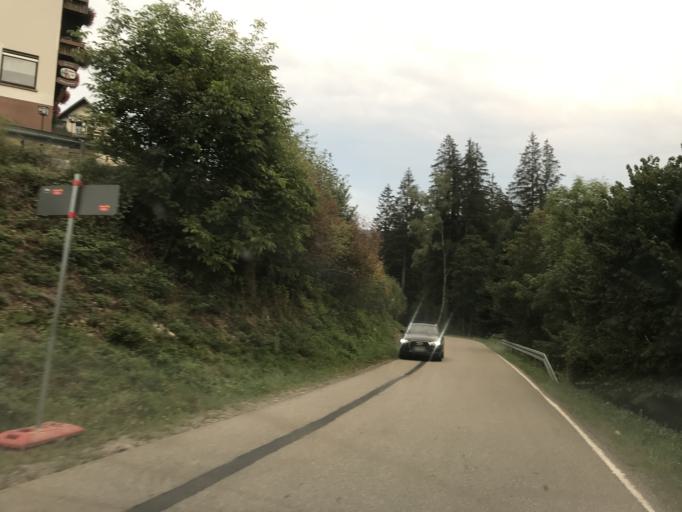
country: DE
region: Baden-Wuerttemberg
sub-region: Freiburg Region
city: Todtmoos
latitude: 47.7212
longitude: 7.9873
